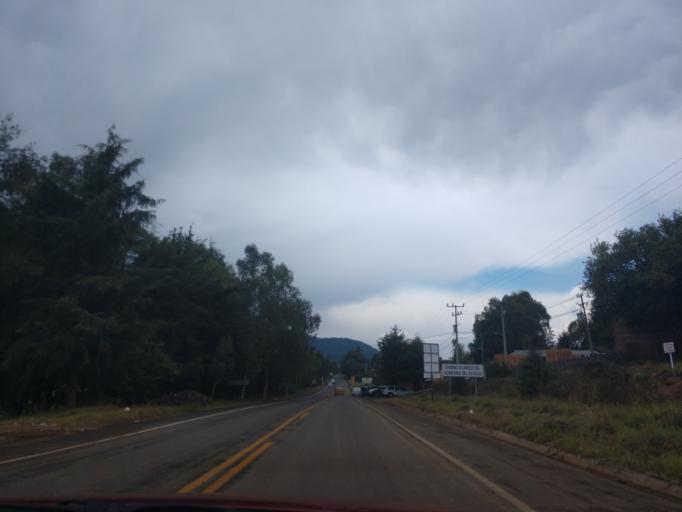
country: MX
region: Jalisco
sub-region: Mazamitla
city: Mazamitla
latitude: 19.9332
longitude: -103.0415
